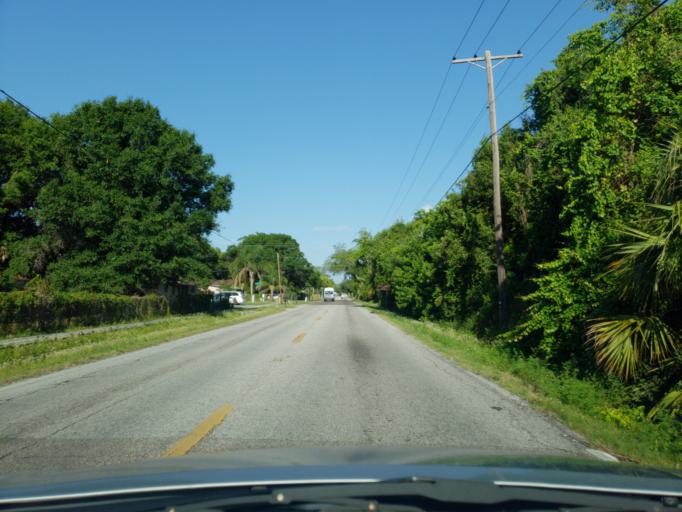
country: US
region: Florida
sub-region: Hillsborough County
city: Palm River-Clair Mel
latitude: 27.9431
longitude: -82.3887
